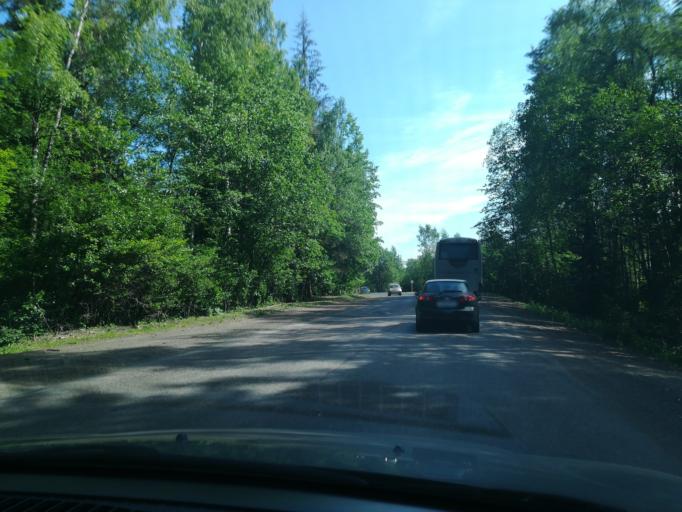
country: RU
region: Leningrad
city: Lesogorskiy
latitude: 61.0648
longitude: 28.9255
